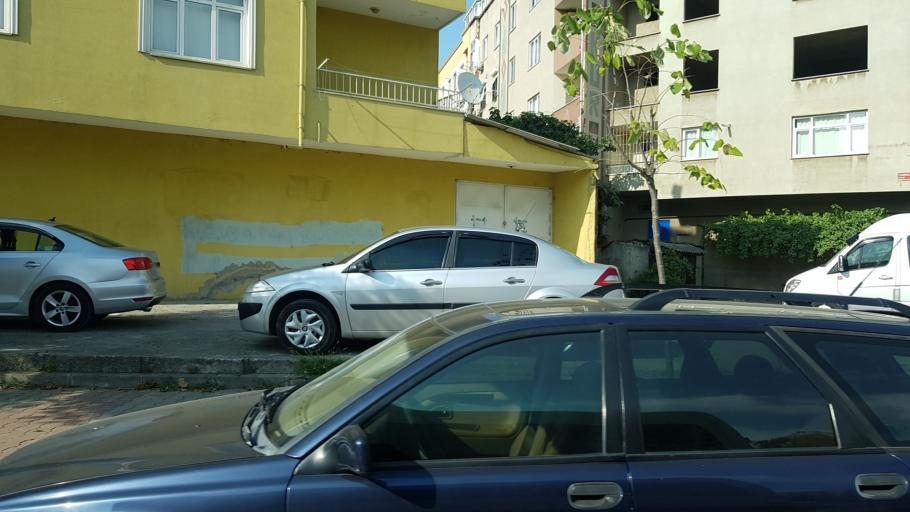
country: TR
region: Istanbul
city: Maltepe
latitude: 40.9069
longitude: 29.1917
